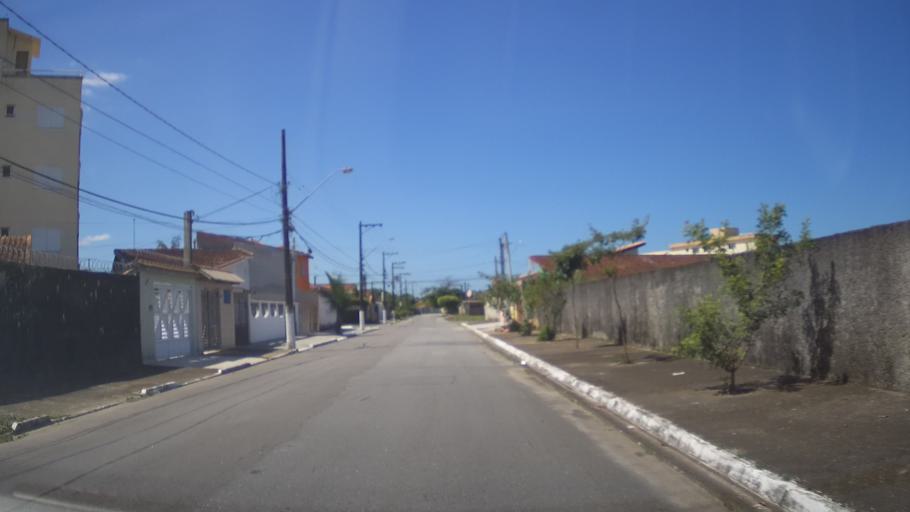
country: BR
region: Sao Paulo
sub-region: Mongagua
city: Mongagua
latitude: -24.0423
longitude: -46.5162
